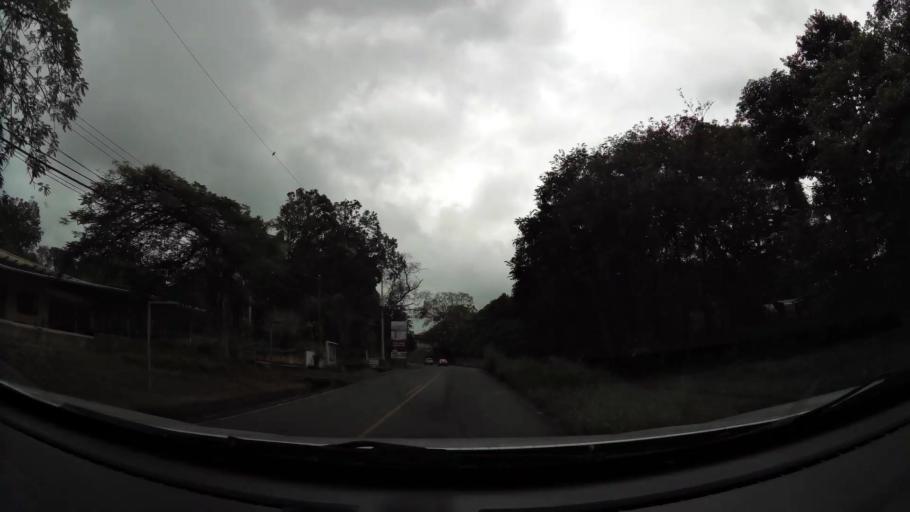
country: CR
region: Puntarenas
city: Esparza
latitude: 9.9946
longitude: -84.6533
